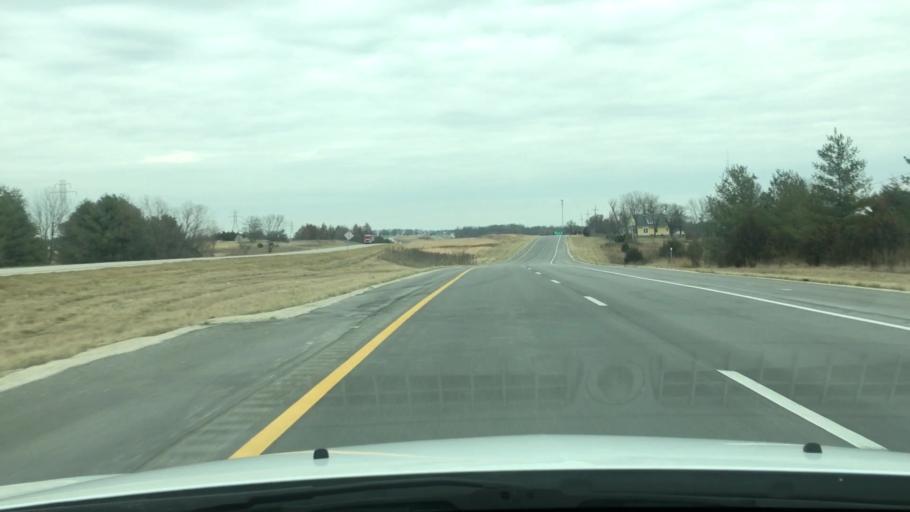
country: US
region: Missouri
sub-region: Audrain County
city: Mexico
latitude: 39.0959
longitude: -91.8986
